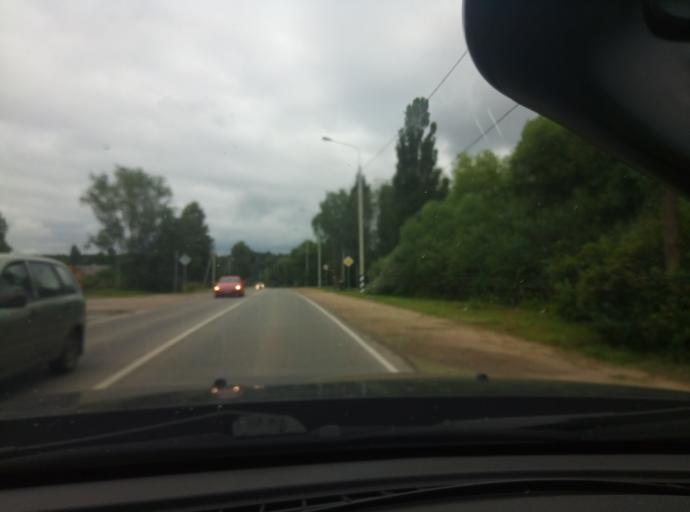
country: RU
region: Kaluga
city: Zhukovo
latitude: 55.0192
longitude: 36.7539
